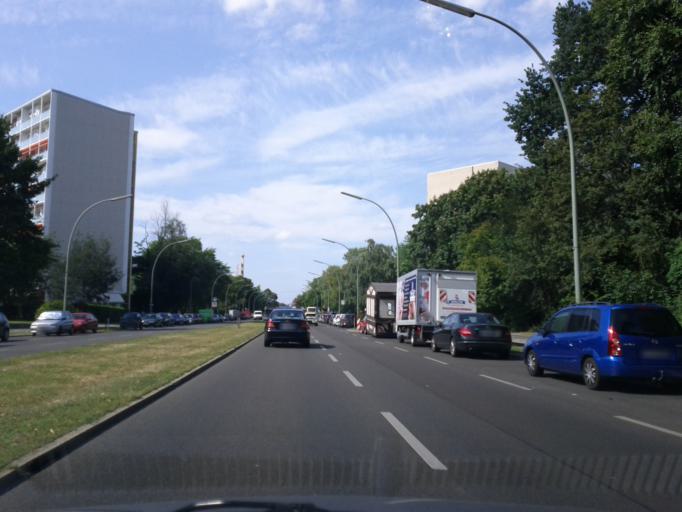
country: DE
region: Berlin
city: Hansaviertel
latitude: 52.5165
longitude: 13.3454
